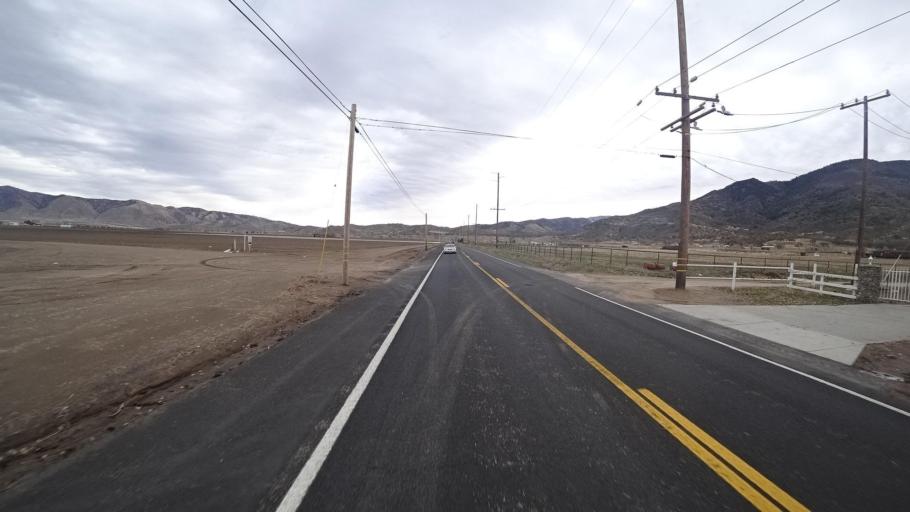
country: US
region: California
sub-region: Kern County
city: Stallion Springs
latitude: 35.0943
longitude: -118.6111
